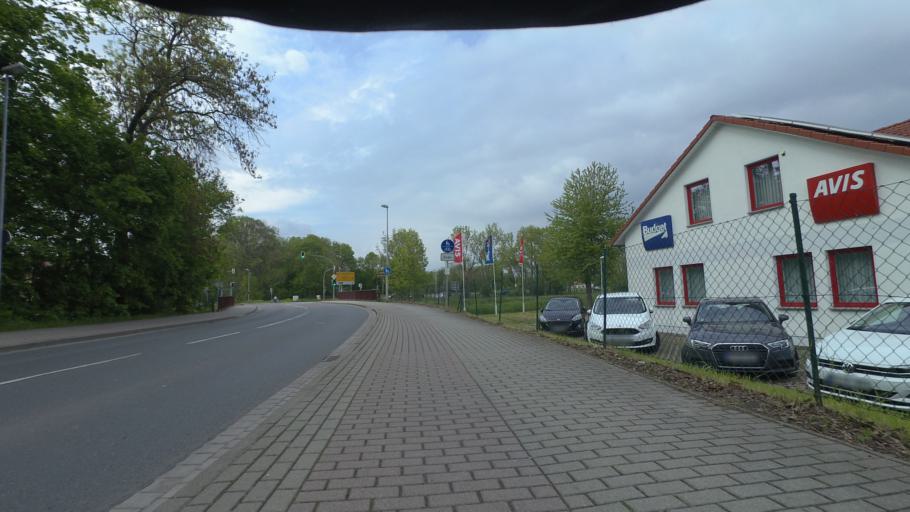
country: DE
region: Saxony-Anhalt
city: Halberstadt
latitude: 51.8966
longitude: 11.0343
